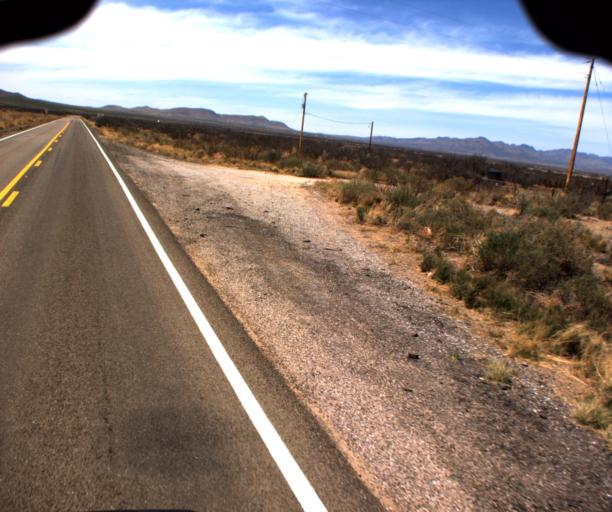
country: US
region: Arizona
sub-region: Cochise County
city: Willcox
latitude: 32.1390
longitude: -109.9182
